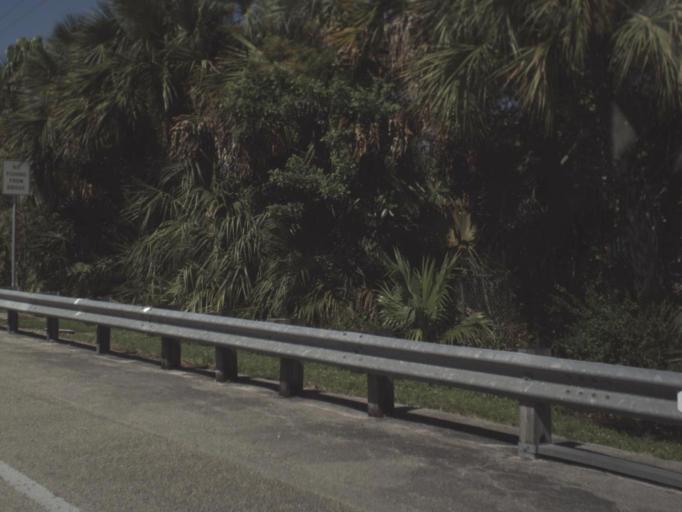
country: US
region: Florida
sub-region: Collier County
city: Marco
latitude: 25.9598
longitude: -81.5089
